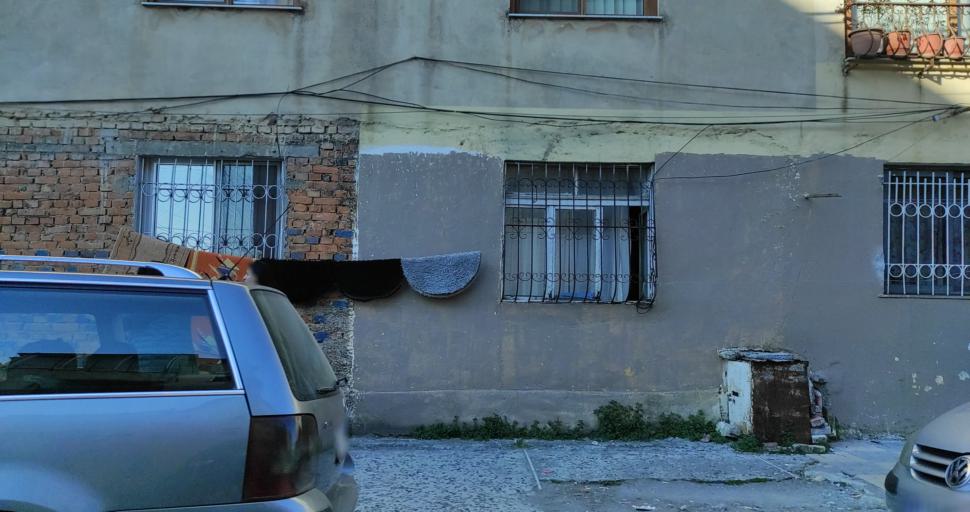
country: AL
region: Shkoder
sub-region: Rrethi i Shkodres
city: Shkoder
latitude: 42.0593
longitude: 19.5141
